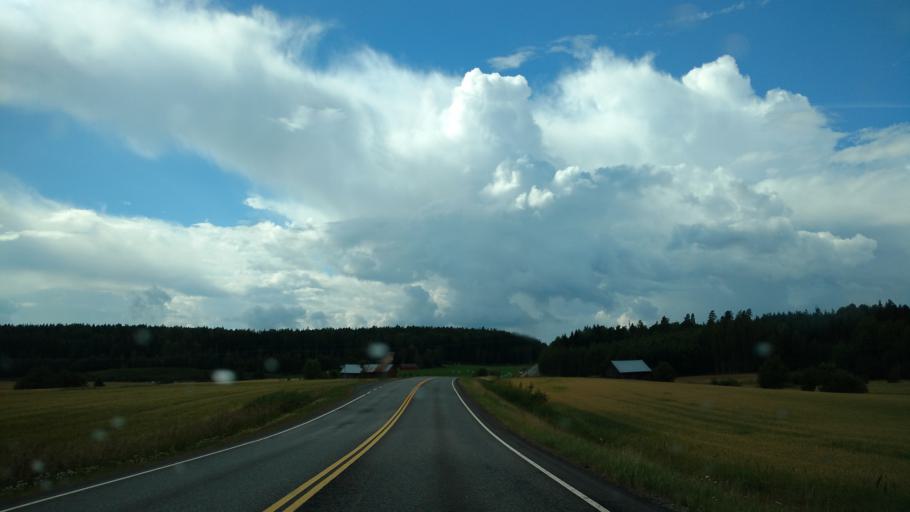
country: FI
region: Varsinais-Suomi
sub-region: Turku
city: Paimio
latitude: 60.4089
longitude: 22.7947
